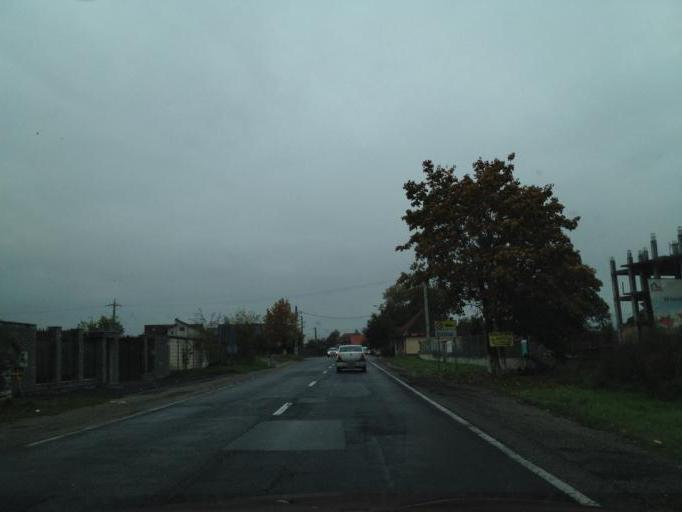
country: RO
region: Brasov
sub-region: Comuna Cristian
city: Cristian
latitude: 45.6335
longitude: 25.4933
